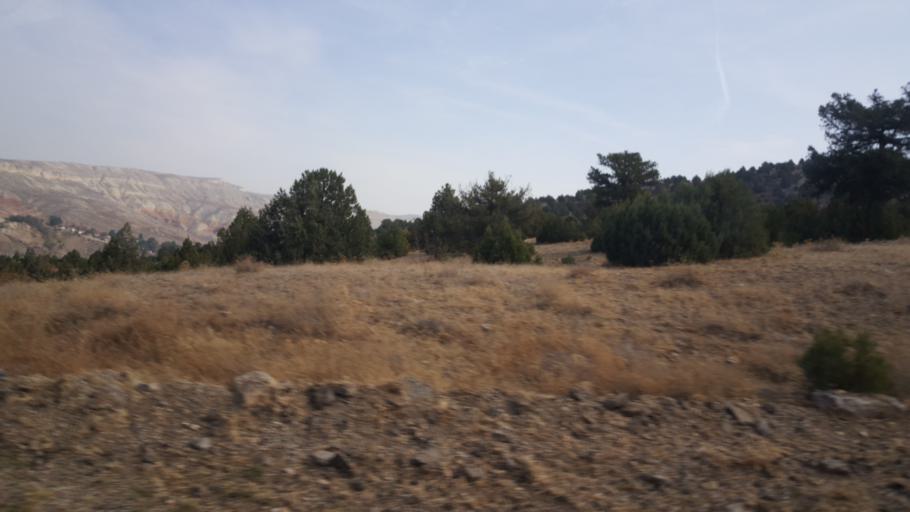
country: TR
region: Ankara
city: Nallihan
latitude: 40.0533
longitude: 31.3990
